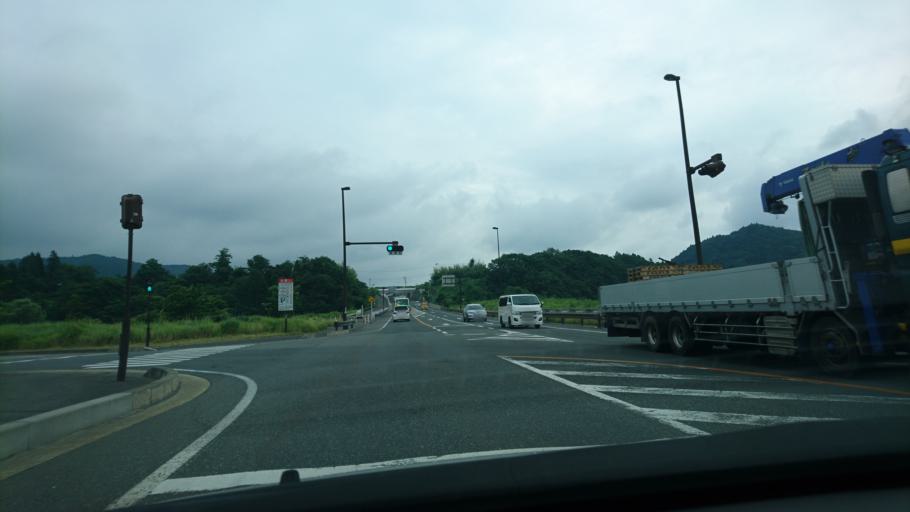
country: JP
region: Miyagi
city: Furukawa
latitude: 38.7334
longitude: 140.7725
